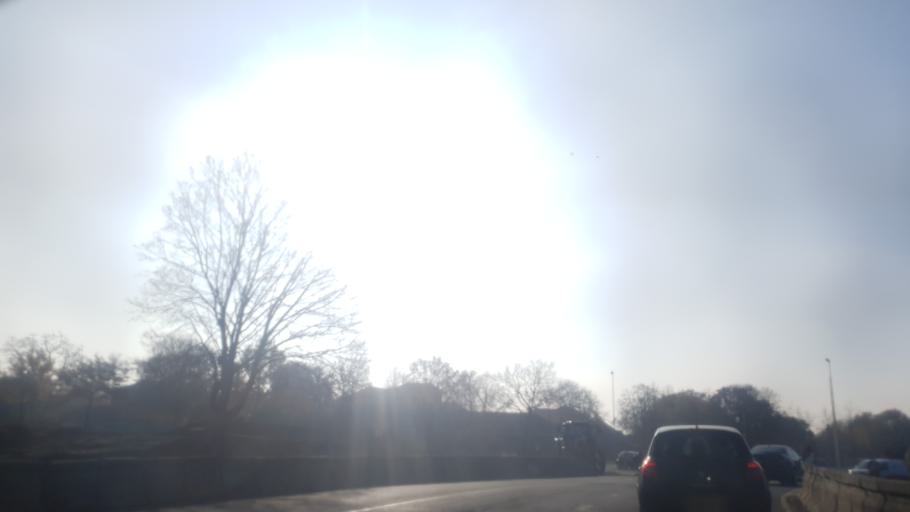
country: NL
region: North Brabant
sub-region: Gemeente Grave
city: Grave
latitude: 51.7490
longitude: 5.7302
